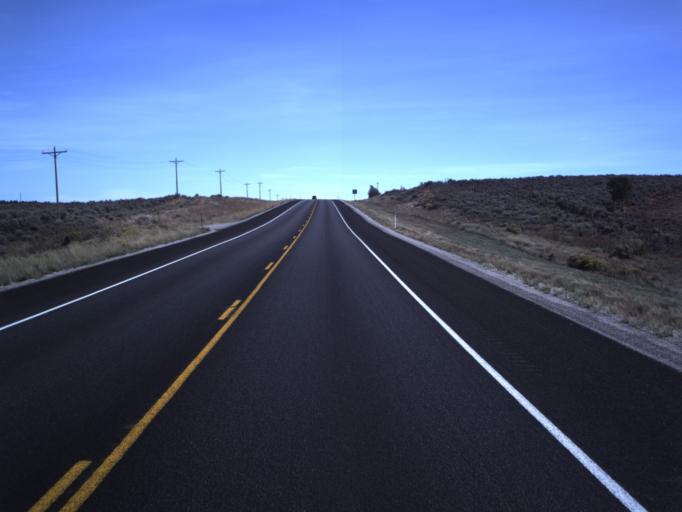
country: US
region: Utah
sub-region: San Juan County
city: Monticello
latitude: 37.8699
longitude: -109.2509
